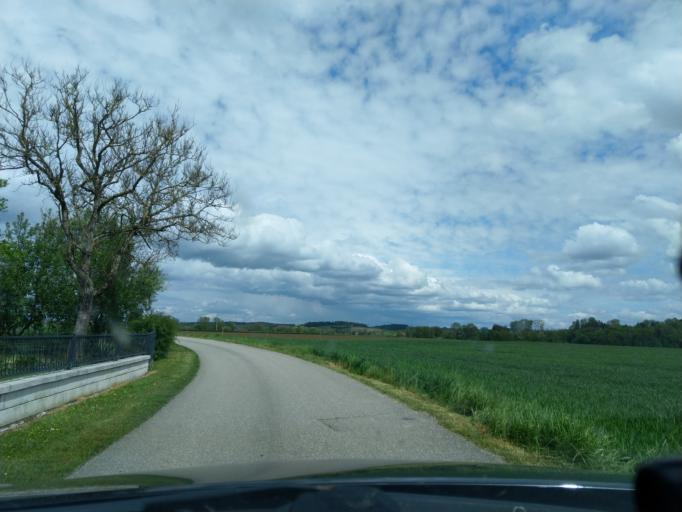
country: DE
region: Bavaria
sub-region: Lower Bavaria
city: Bad Fussing
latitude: 48.2791
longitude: 13.3207
